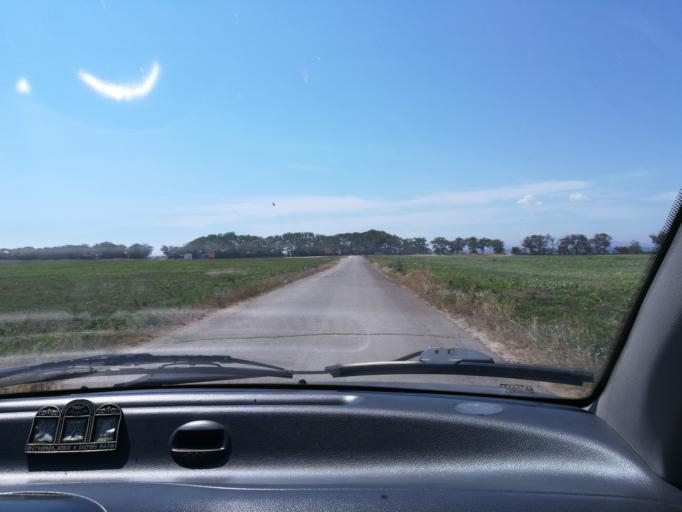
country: RU
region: Krasnodarskiy
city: Blagovetschenskaya
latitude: 45.0677
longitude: 37.0581
